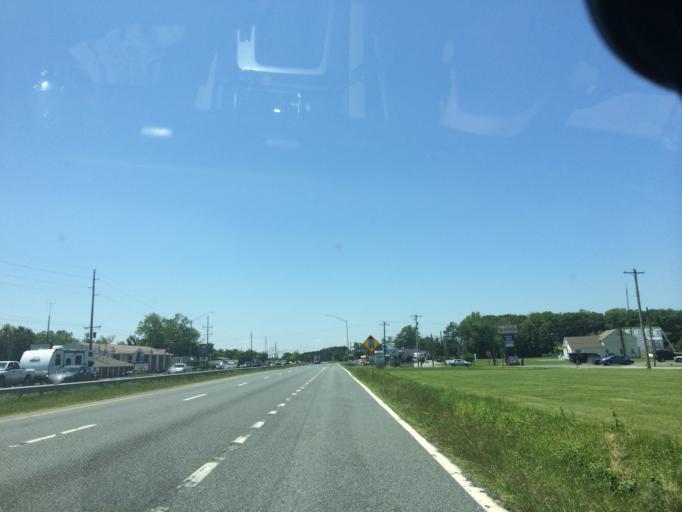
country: US
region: Maryland
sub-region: Dorchester County
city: Cambridge
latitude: 38.5527
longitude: -76.0385
